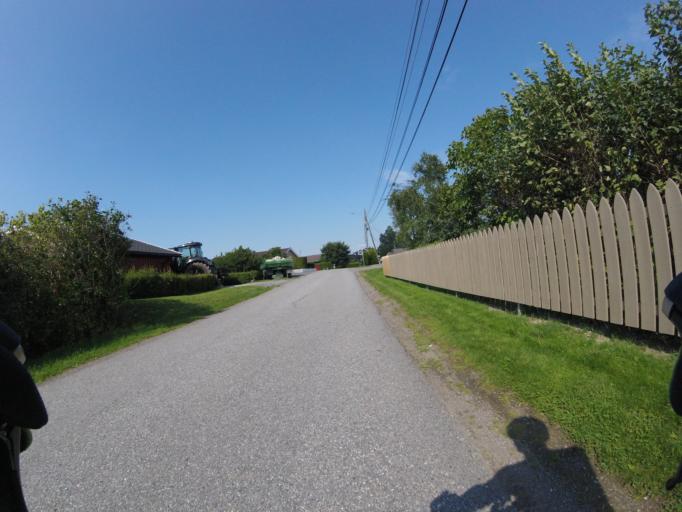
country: NO
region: Akershus
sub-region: Sorum
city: Frogner
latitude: 60.0243
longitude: 11.1148
